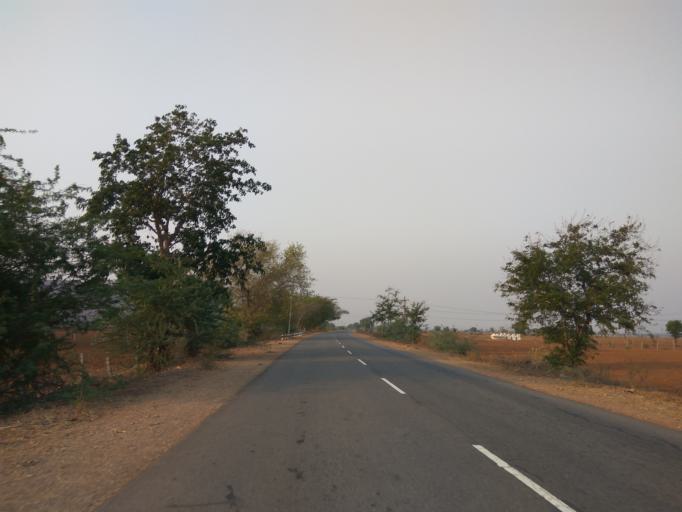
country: IN
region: Andhra Pradesh
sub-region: Prakasam
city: Cumbum
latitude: 15.6475
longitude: 79.1461
